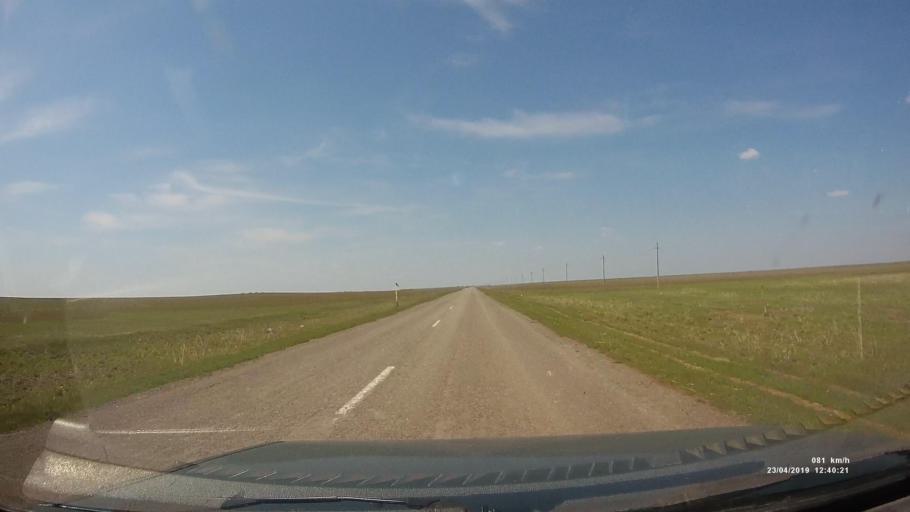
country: RU
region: Kalmykiya
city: Yashalta
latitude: 46.4398
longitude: 42.6975
